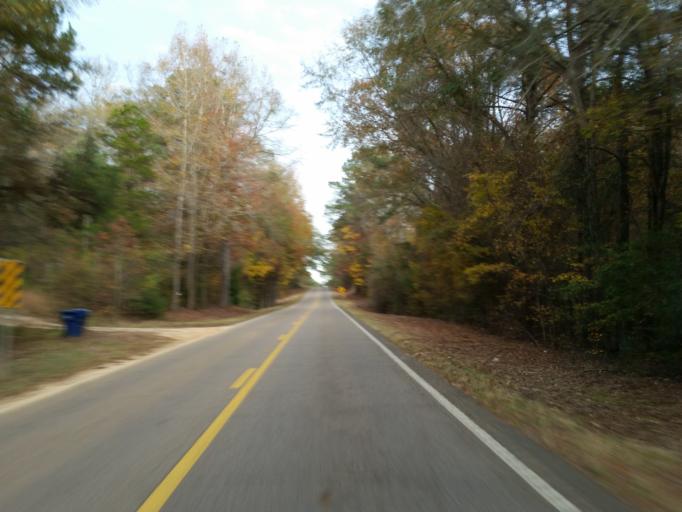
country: US
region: Mississippi
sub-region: Lauderdale County
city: Marion
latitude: 32.4216
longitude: -88.4844
